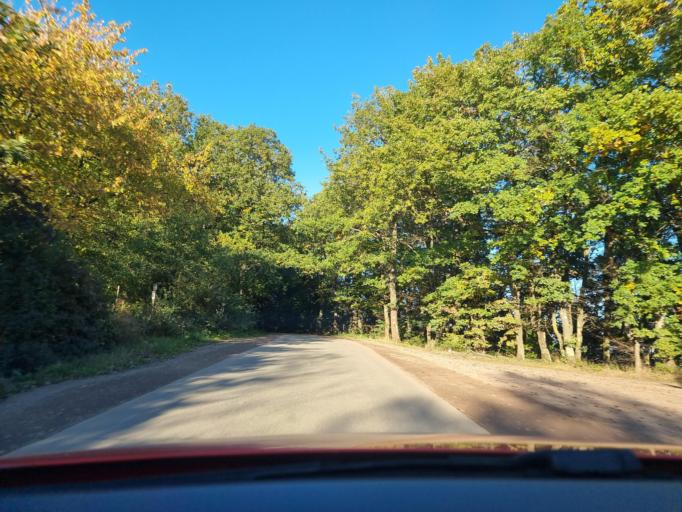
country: DE
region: Rheinland-Pfalz
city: Klausen
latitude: 49.8855
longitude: 6.8942
